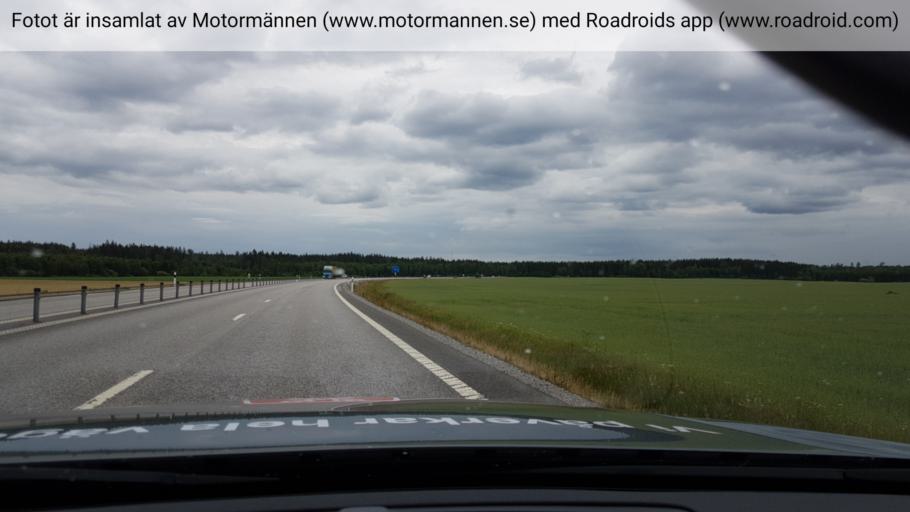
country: SE
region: Vaestmanland
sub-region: Surahammars Kommun
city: Ramnas
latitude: 59.7539
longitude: 16.2215
